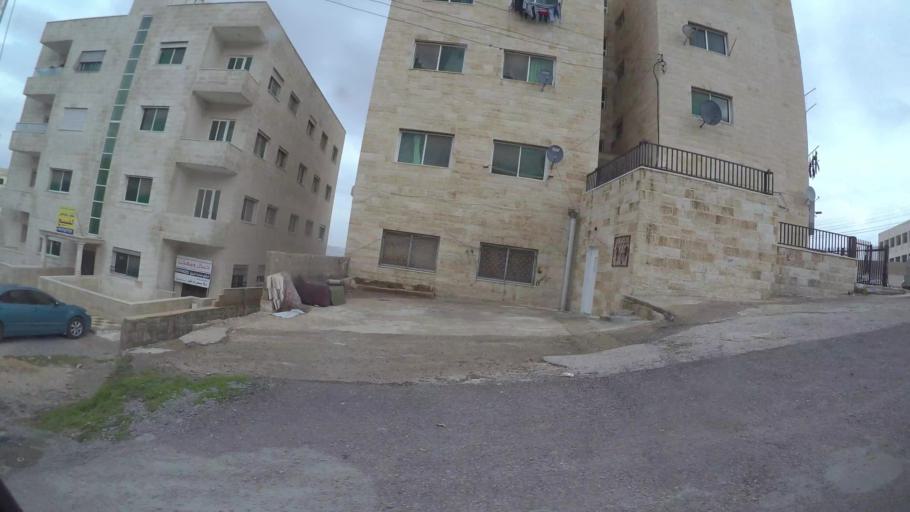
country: JO
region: Amman
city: Al Jubayhah
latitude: 32.0355
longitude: 35.8288
